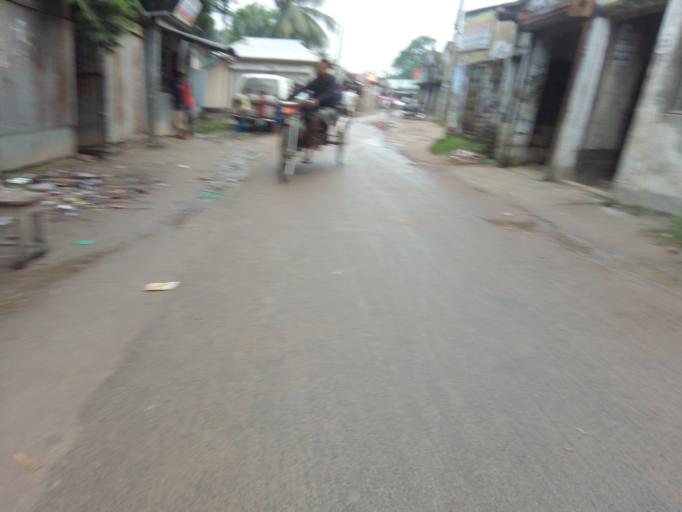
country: BD
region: Khulna
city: Kalia
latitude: 23.2150
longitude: 89.6971
